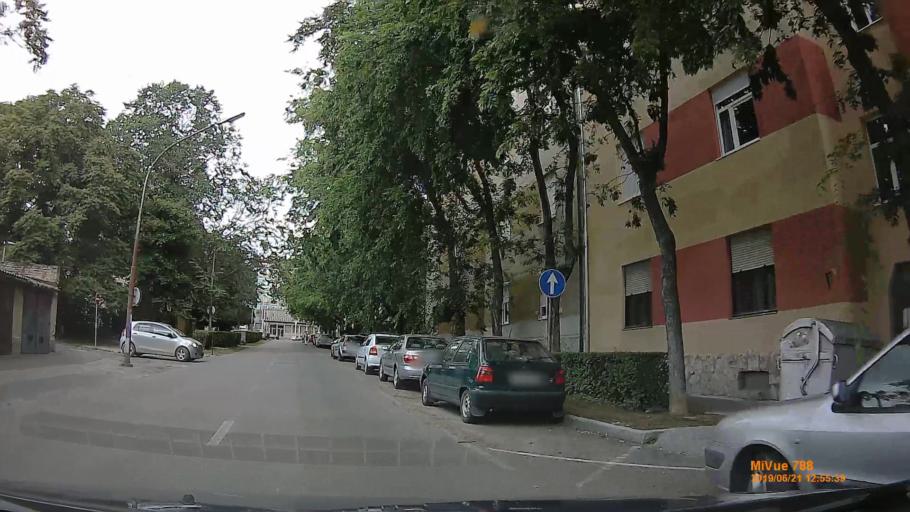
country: HU
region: Baranya
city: Pecs
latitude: 46.0733
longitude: 18.2362
